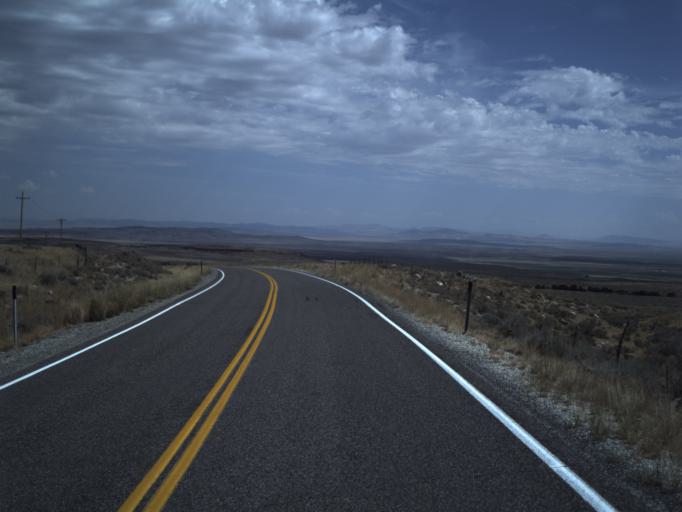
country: US
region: Idaho
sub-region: Cassia County
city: Burley
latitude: 41.8149
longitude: -113.2152
